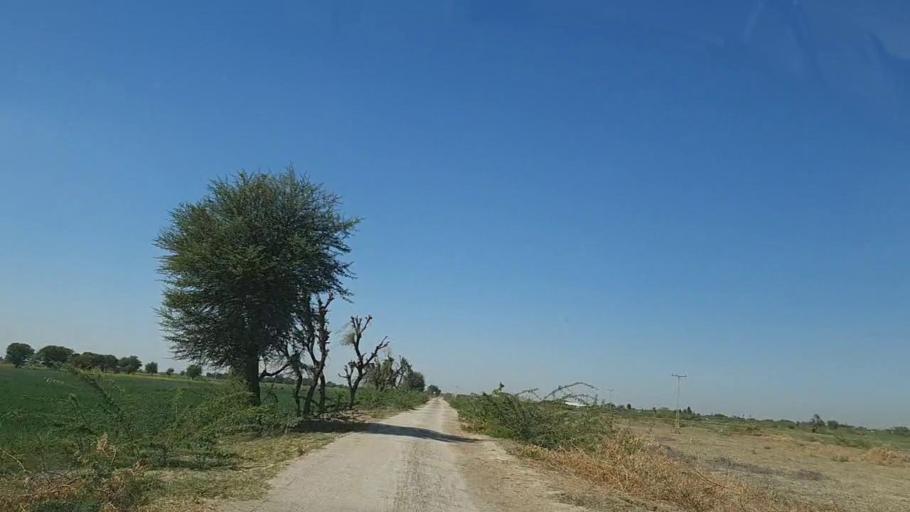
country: PK
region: Sindh
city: Dhoro Naro
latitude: 25.4890
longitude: 69.5167
